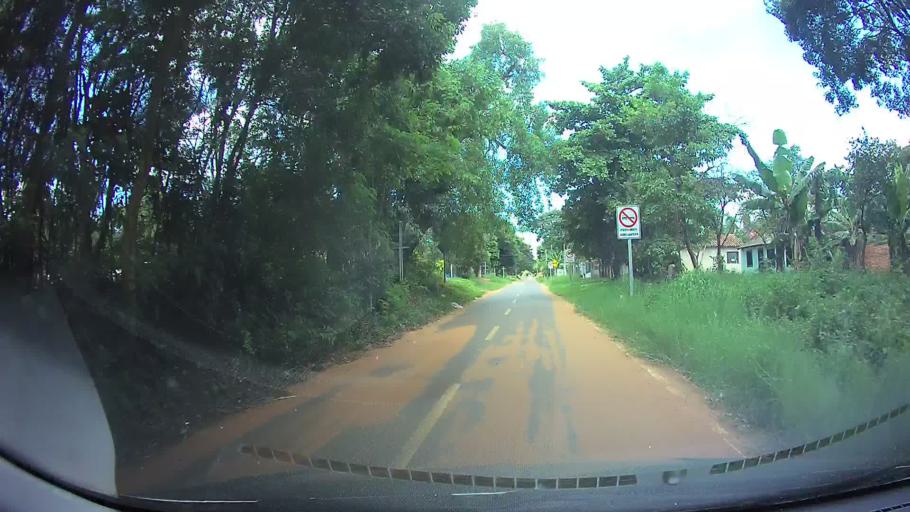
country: PY
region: Central
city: Aregua
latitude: -25.2928
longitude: -57.4239
